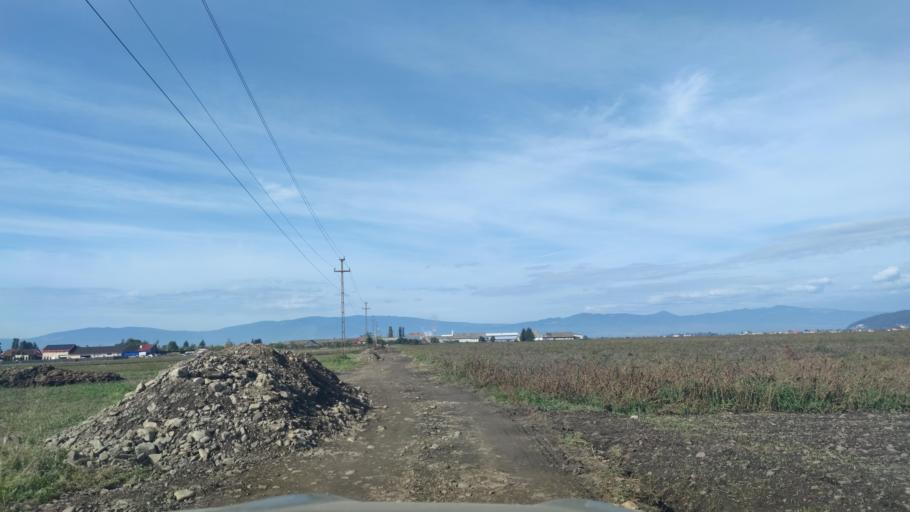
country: RO
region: Harghita
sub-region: Municipiul Gheorgheni
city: Gheorgheni
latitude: 46.7234
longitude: 25.5821
